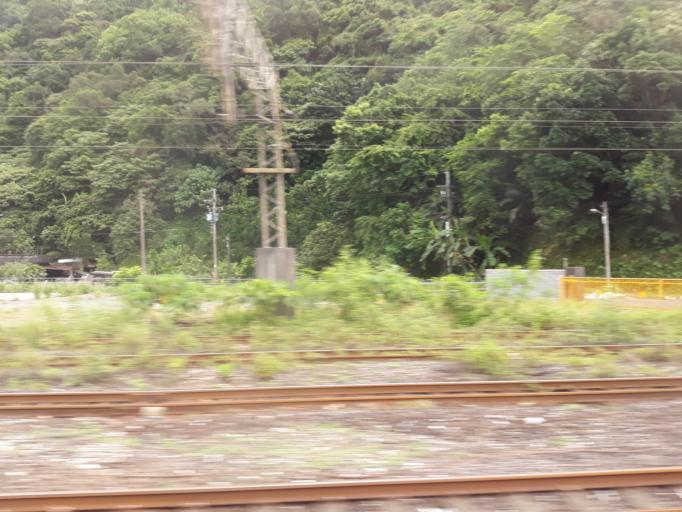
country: TW
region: Taiwan
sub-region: Yilan
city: Yilan
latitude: 24.5675
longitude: 121.8439
